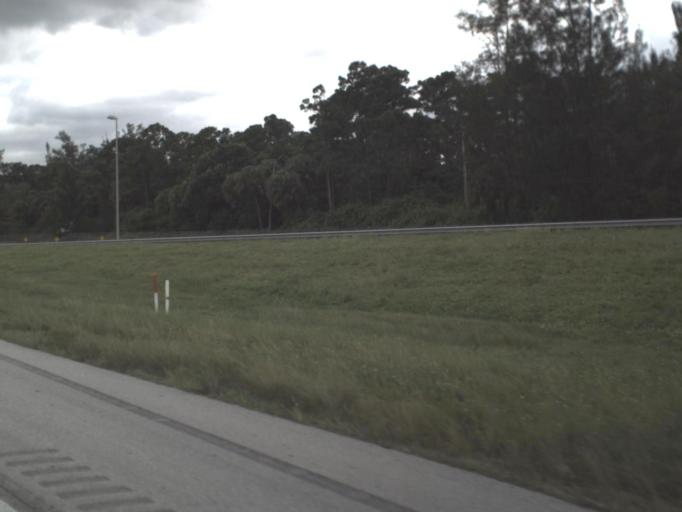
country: US
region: Florida
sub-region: Palm Beach County
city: Plantation Mobile Home Park
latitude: 26.6993
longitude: -80.1494
